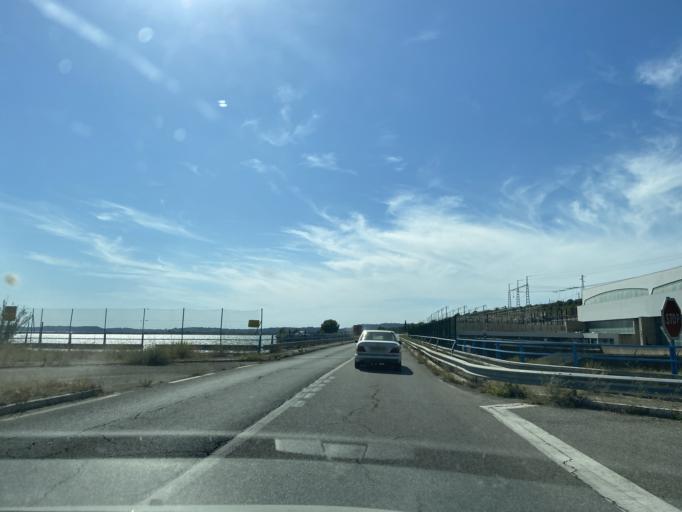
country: FR
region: Provence-Alpes-Cote d'Azur
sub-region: Departement des Bouches-du-Rhone
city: Cornillon-Confoux
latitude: 43.5267
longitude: 5.0743
